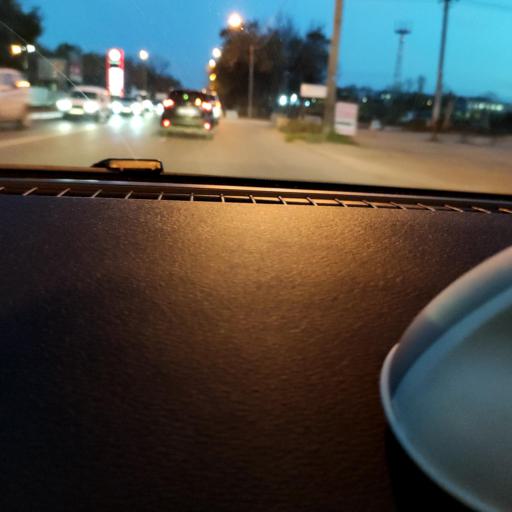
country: RU
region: Samara
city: Samara
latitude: 53.2213
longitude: 50.2028
